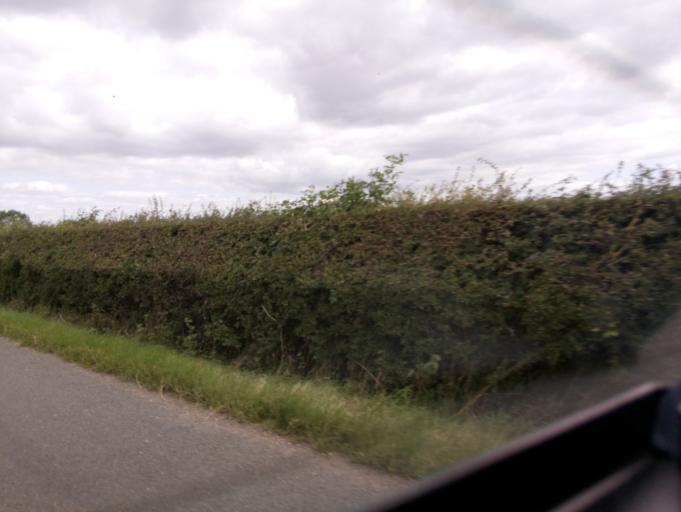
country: GB
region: England
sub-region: Buckinghamshire
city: Newton Longville
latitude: 51.9672
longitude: -0.8169
